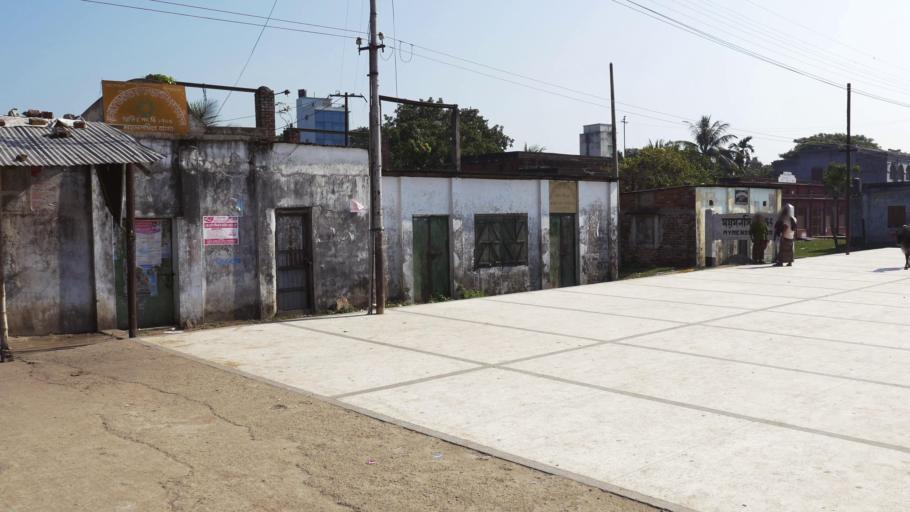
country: BD
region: Dhaka
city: Mymensingh
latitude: 24.6942
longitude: 90.4531
